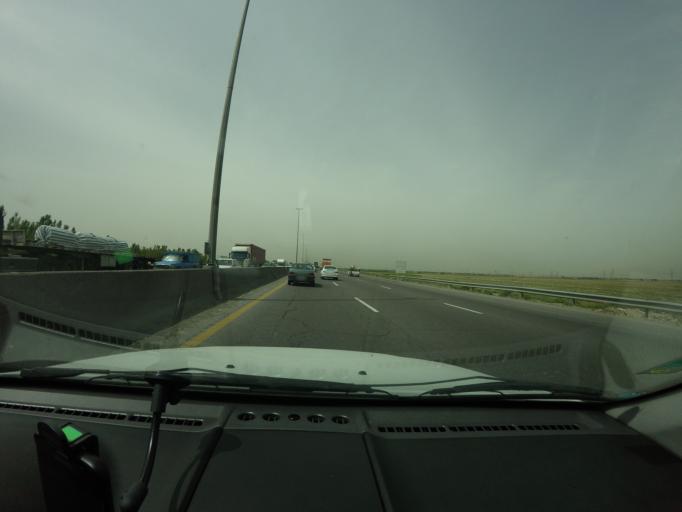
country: IR
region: Tehran
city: Eslamshahr
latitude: 35.6063
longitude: 51.1974
